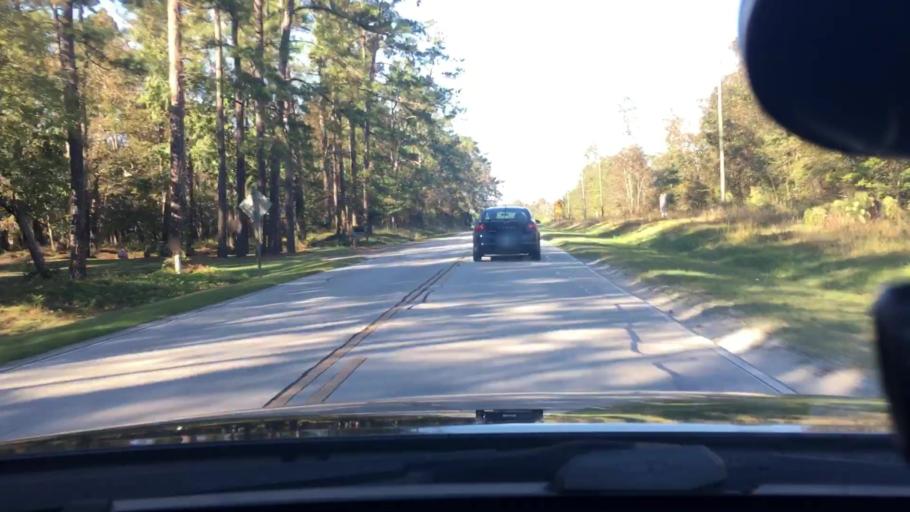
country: US
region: North Carolina
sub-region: Craven County
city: Vanceboro
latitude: 35.2767
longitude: -77.1532
